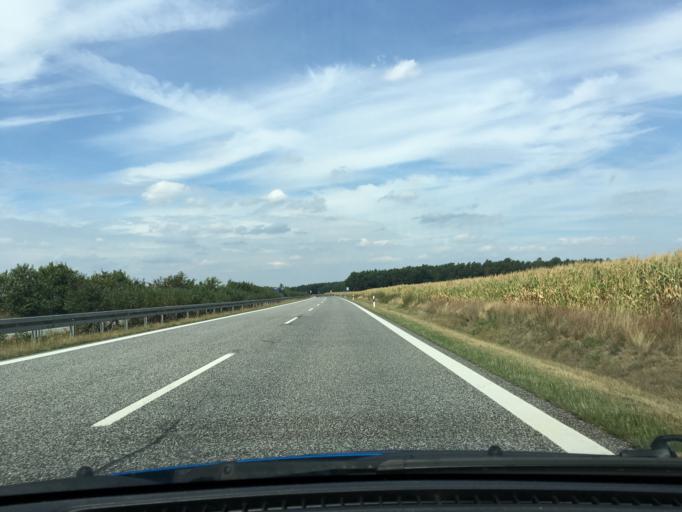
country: DE
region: Mecklenburg-Vorpommern
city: Mirow
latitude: 53.4809
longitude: 11.4882
